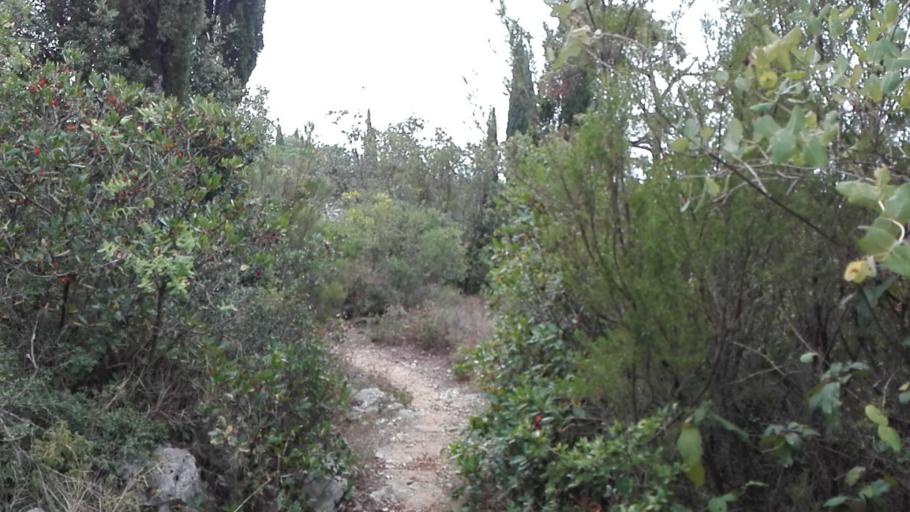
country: ME
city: Igalo
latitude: 42.4858
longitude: 18.4043
